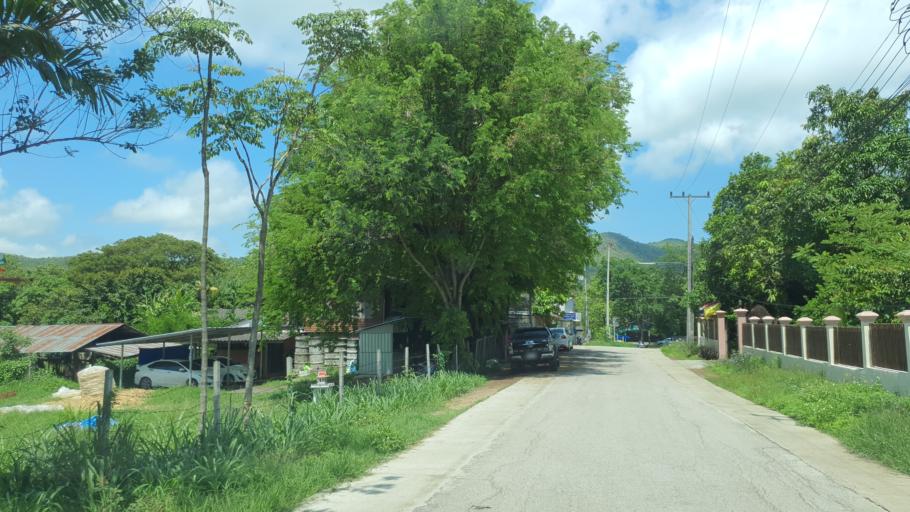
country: TH
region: Chiang Mai
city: Mae On
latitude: 18.7956
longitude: 99.2457
